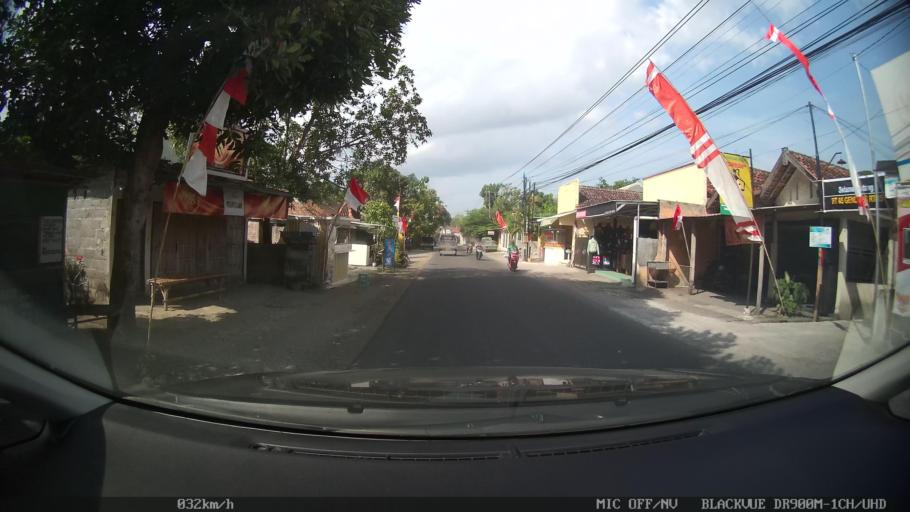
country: ID
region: Daerah Istimewa Yogyakarta
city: Kasihan
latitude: -7.8396
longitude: 110.3142
